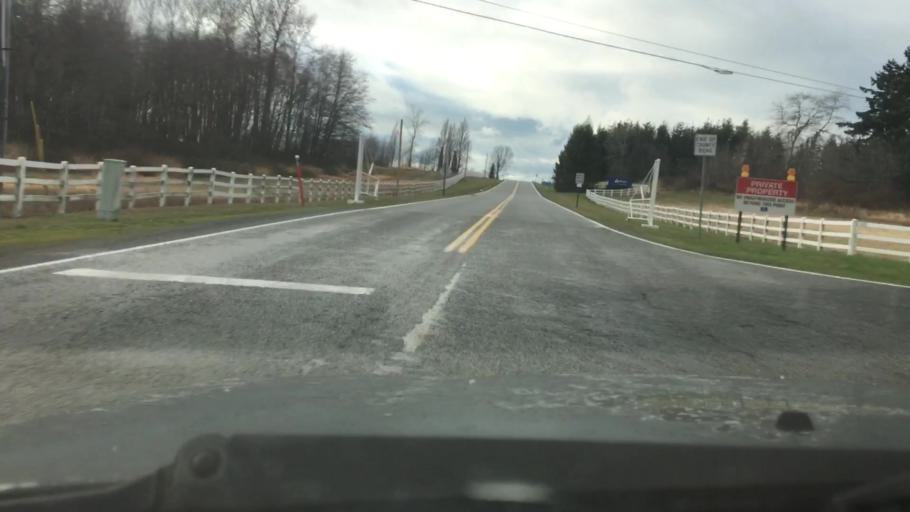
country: US
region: Washington
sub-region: Whatcom County
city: Birch Bay
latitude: 48.8485
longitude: -122.6941
